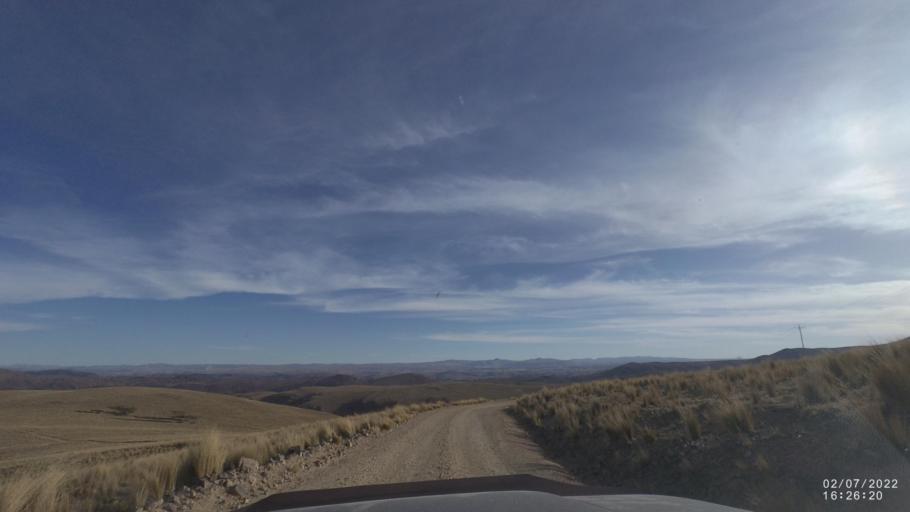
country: BO
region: Cochabamba
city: Irpa Irpa
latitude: -17.9470
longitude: -66.4652
